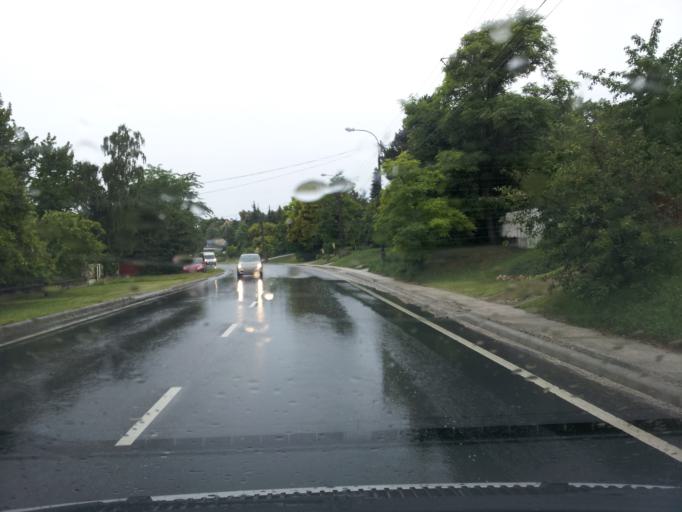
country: HU
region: Veszprem
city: Balatonkenese
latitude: 47.0227
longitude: 18.1476
